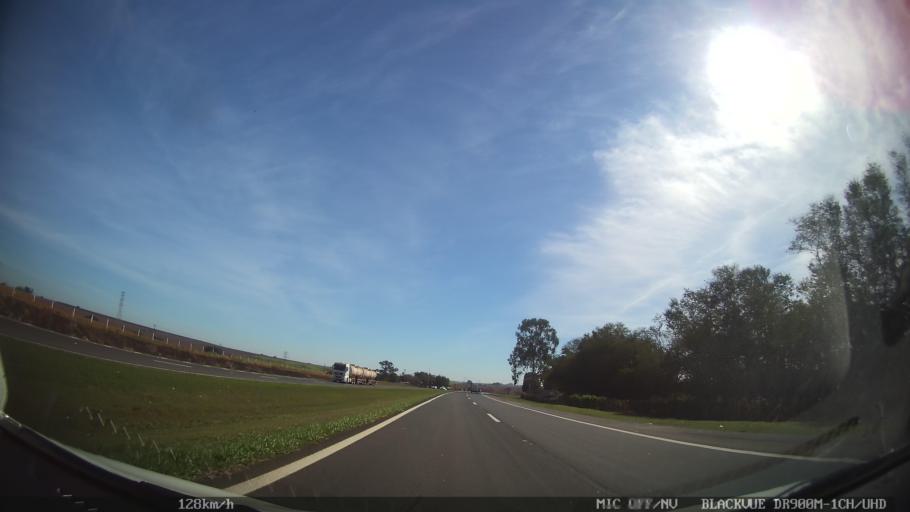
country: BR
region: Sao Paulo
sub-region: Leme
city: Leme
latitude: -22.1374
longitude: -47.4079
